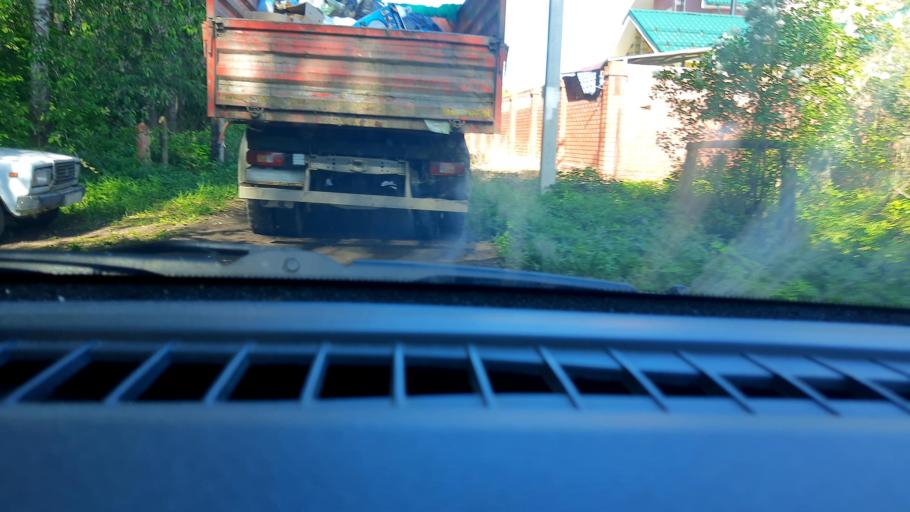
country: RU
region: Nizjnij Novgorod
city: Afonino
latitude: 56.1973
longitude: 44.0400
